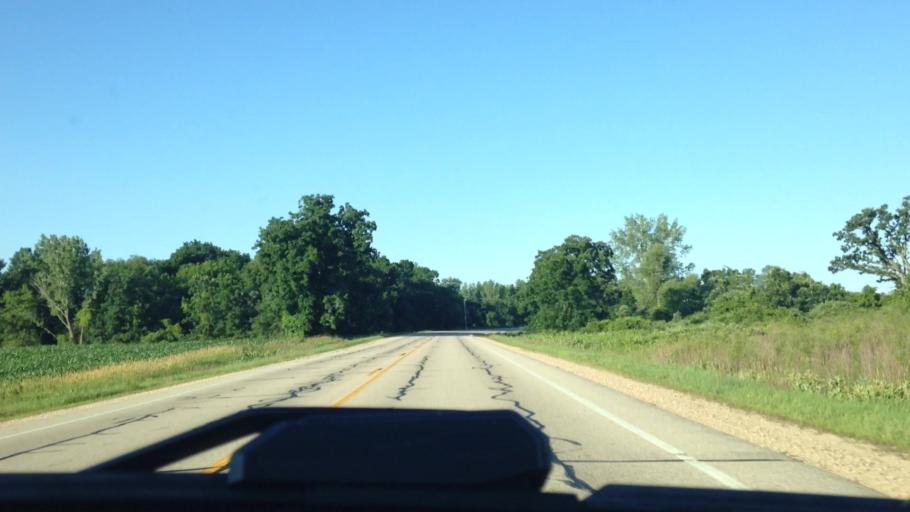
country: US
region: Wisconsin
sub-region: Columbia County
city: Rio
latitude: 43.3360
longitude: -89.2581
